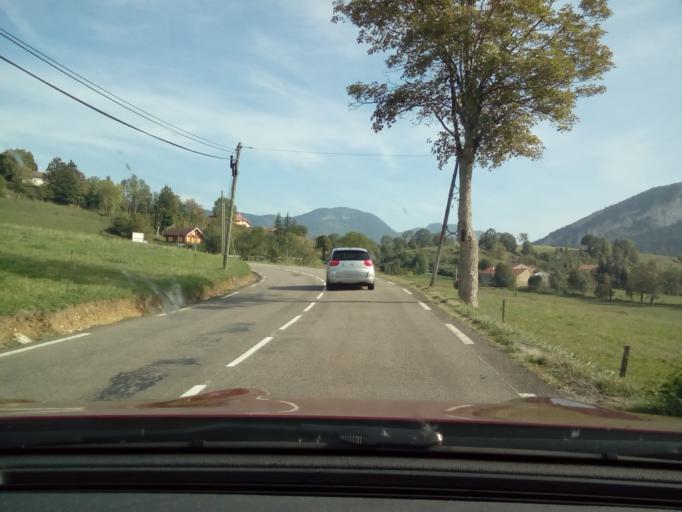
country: FR
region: Rhone-Alpes
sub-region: Departement de la Drome
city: Saint-Laurent-en-Royans
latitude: 44.9722
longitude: 5.4044
